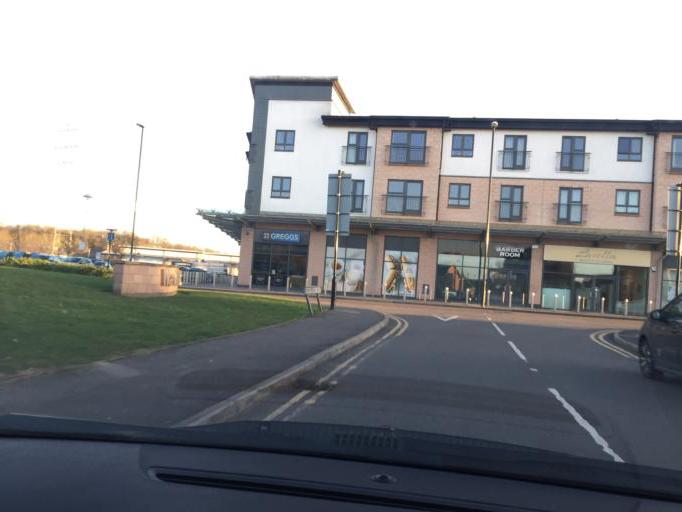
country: GB
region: England
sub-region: Warwickshire
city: Ryton on Dunsmore
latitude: 52.3987
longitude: -1.4337
